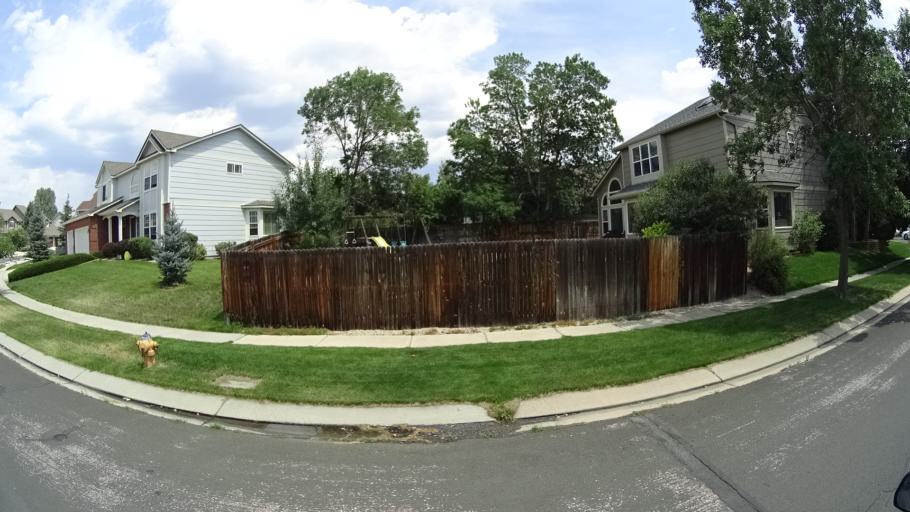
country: US
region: Colorado
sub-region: El Paso County
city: Black Forest
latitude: 38.9610
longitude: -104.7687
